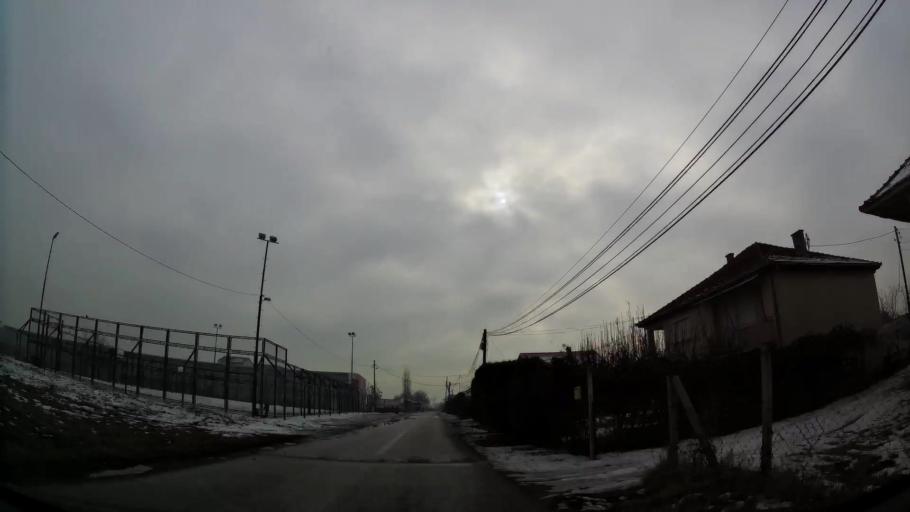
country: MK
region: Ilinden
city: Ilinden
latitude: 41.9949
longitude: 21.5647
